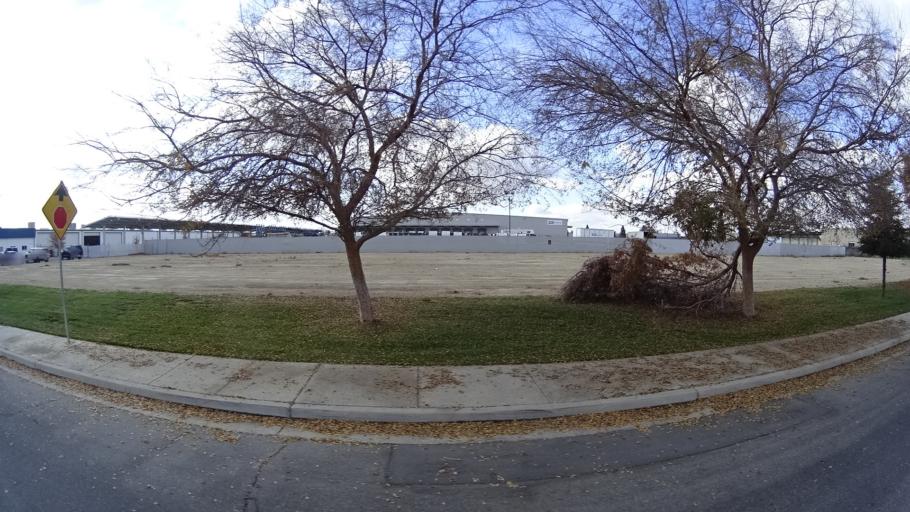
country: US
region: California
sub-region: Kern County
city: Bakersfield
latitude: 35.3490
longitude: -118.9677
